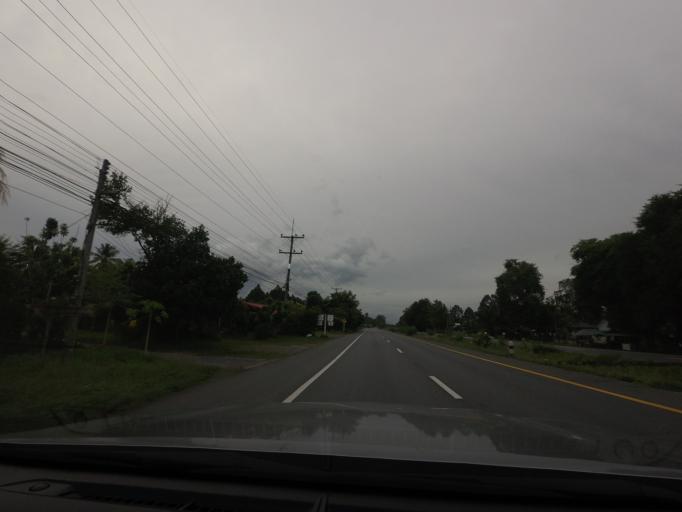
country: TH
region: Nakhon Si Thammarat
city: Chaloem Phra Kiat
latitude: 8.1538
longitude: 100.0589
